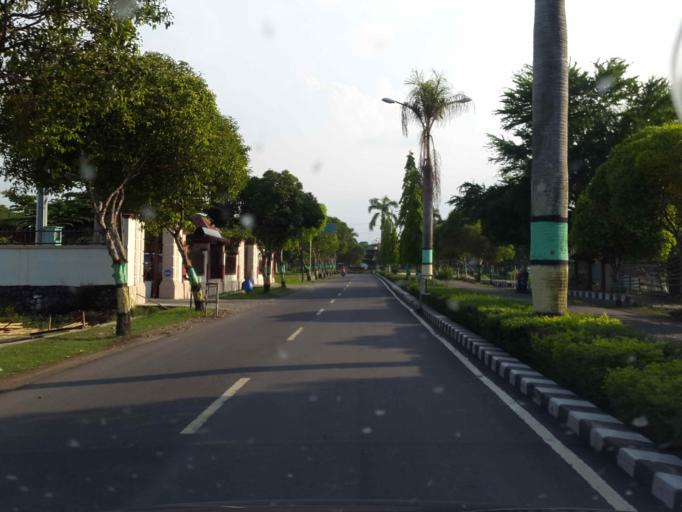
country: ID
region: Central Java
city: Slawi
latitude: -6.9905
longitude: 109.1277
